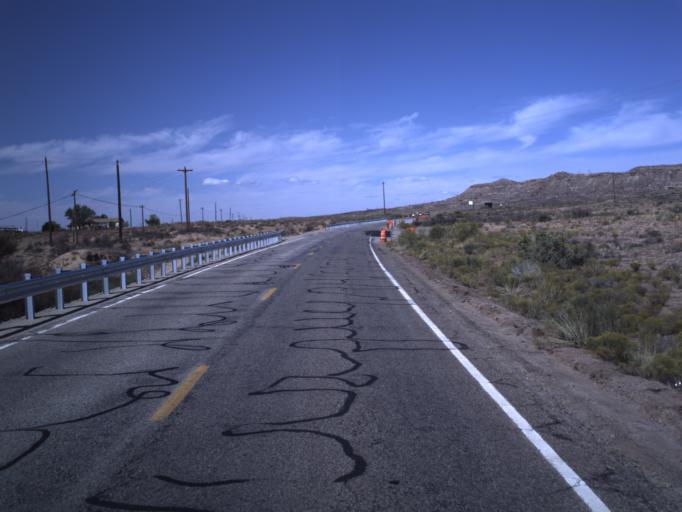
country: US
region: Colorado
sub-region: Montezuma County
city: Towaoc
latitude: 37.2258
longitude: -109.2089
